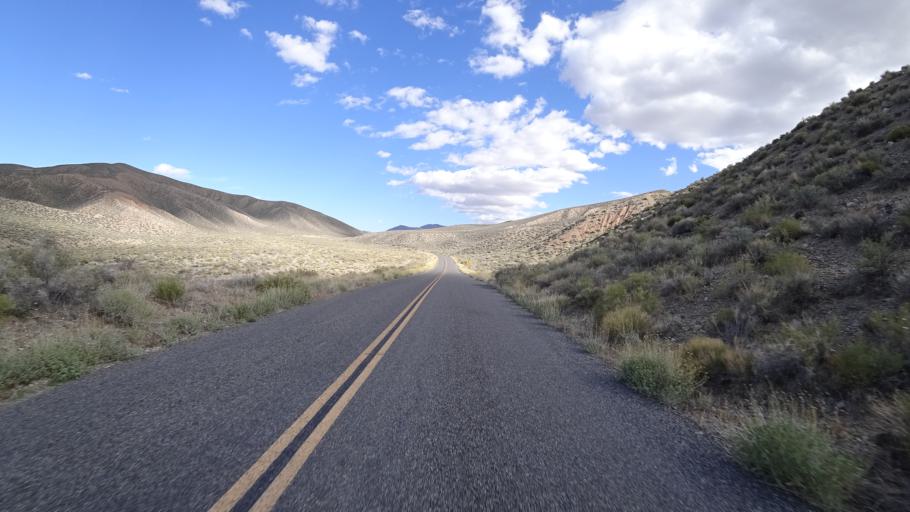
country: US
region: Nevada
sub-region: Nye County
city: Beatty
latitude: 36.4054
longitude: -117.1711
